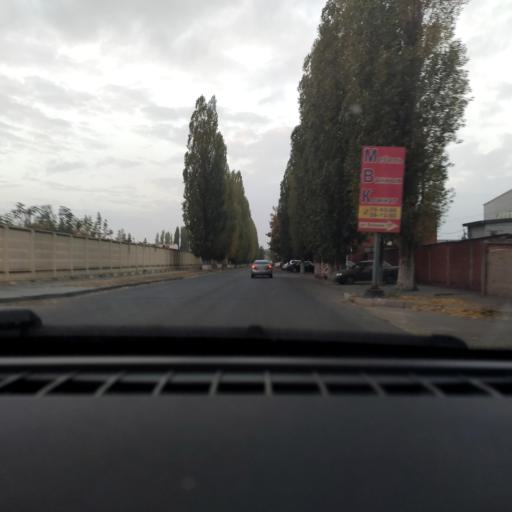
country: RU
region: Voronezj
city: Voronezh
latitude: 51.6512
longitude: 39.2804
